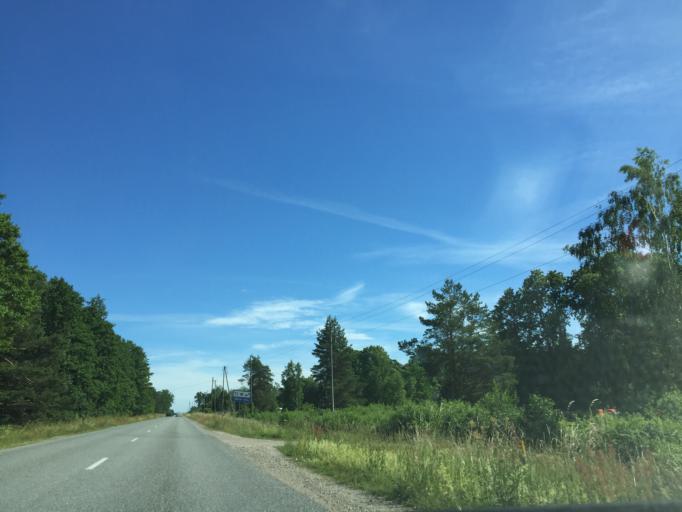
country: LV
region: Rojas
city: Roja
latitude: 57.4780
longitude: 22.8619
